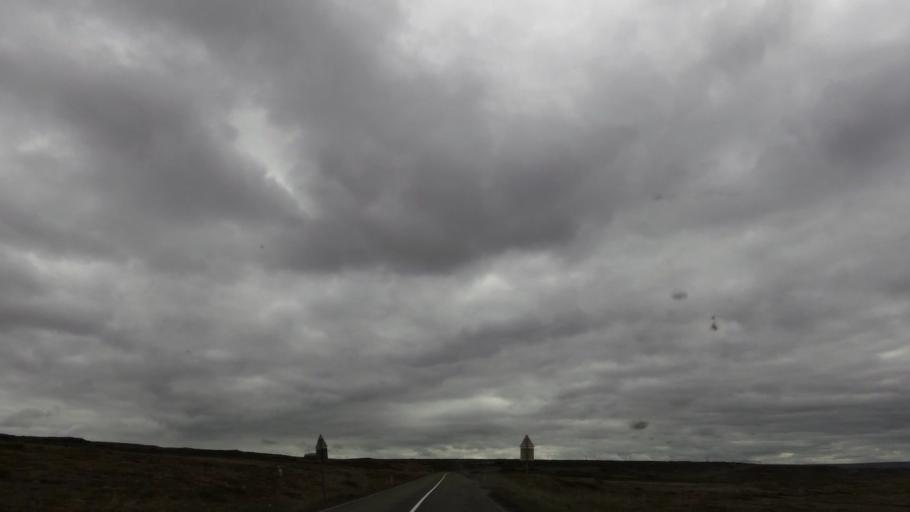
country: IS
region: West
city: Borgarnes
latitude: 65.2086
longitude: -21.7226
